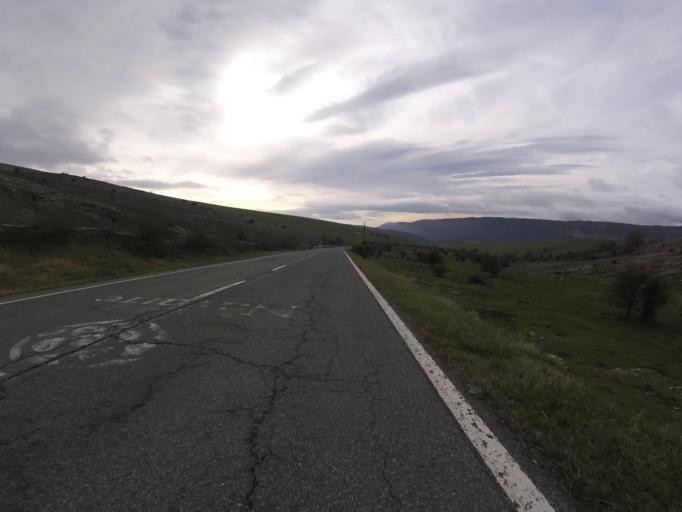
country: ES
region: Navarre
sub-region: Provincia de Navarra
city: Arbizu
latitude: 42.8558
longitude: -2.0132
